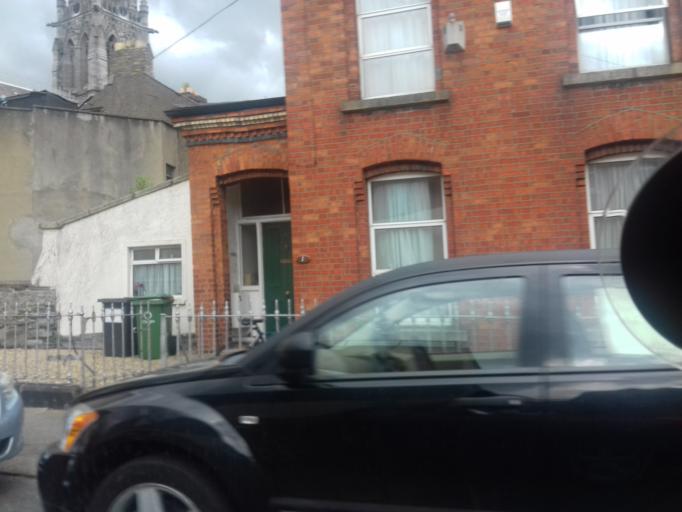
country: IE
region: Leinster
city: Cabra
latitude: 53.3600
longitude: -6.2765
